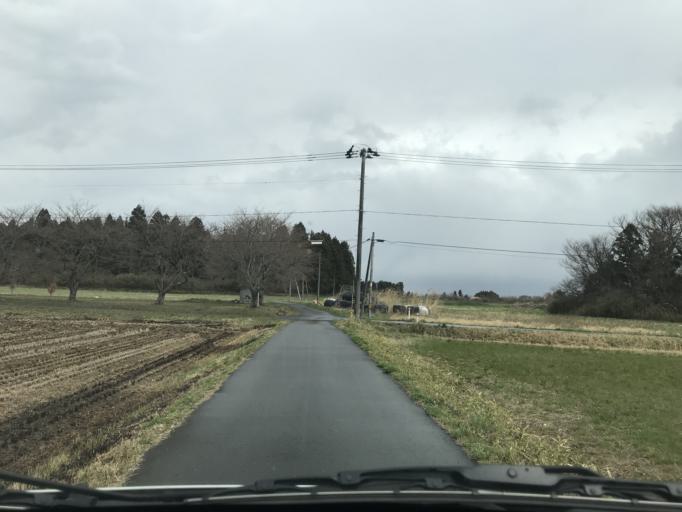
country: JP
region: Iwate
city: Mizusawa
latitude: 39.0988
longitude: 141.1041
